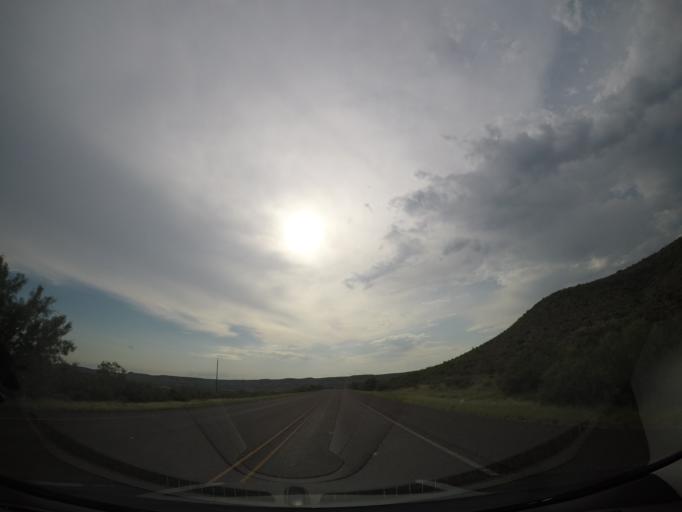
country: US
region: Texas
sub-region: Terrell County
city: Sanderson
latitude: 29.9056
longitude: -101.8150
